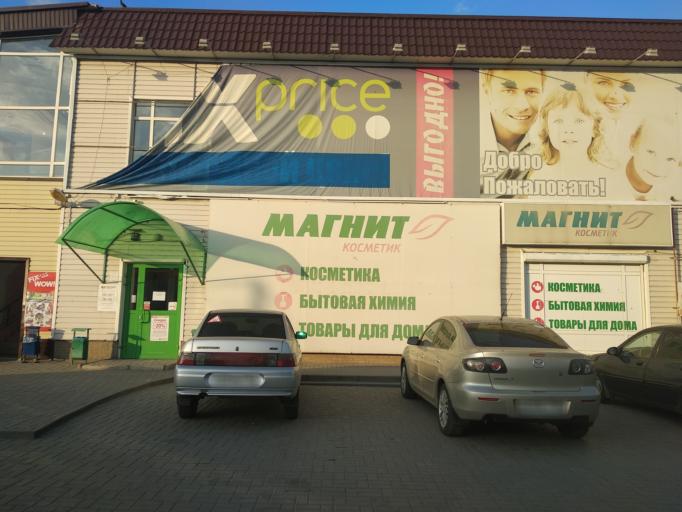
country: RU
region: Rostov
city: Millerovo
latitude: 48.9251
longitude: 40.4013
